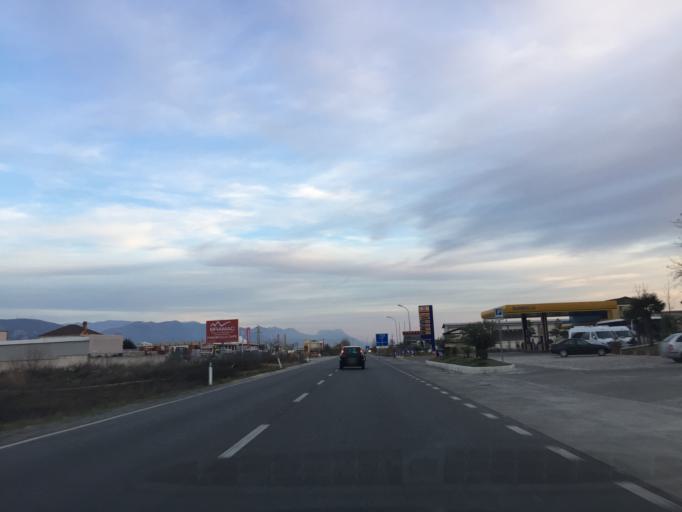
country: AL
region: Lezhe
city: Lezhe
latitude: 41.7510
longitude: 19.6440
